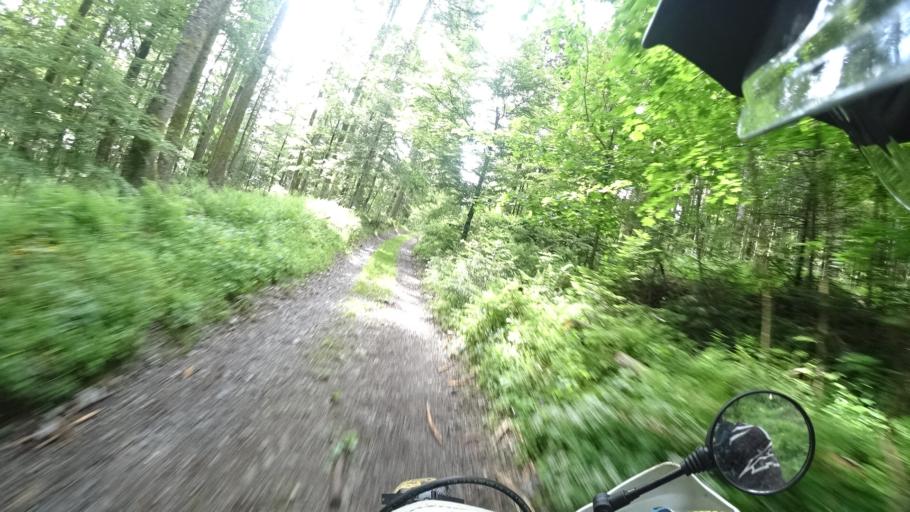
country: HR
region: Primorsko-Goranska
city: Bribir
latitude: 45.2603
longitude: 14.9152
